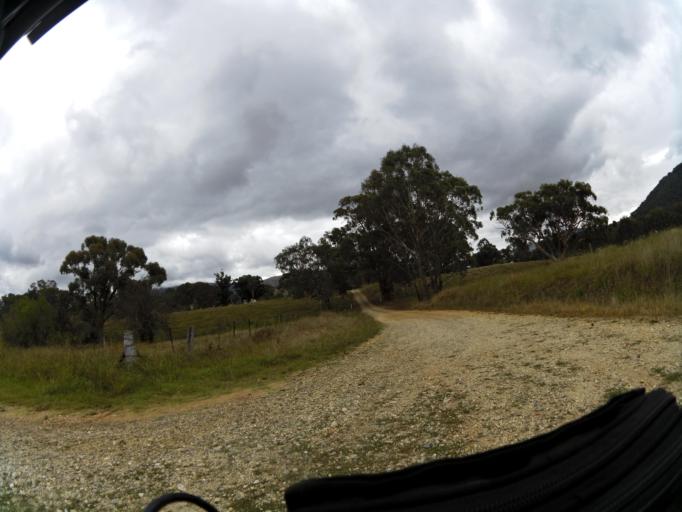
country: AU
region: New South Wales
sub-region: Albury Municipality
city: East Albury
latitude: -36.1919
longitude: 147.3347
